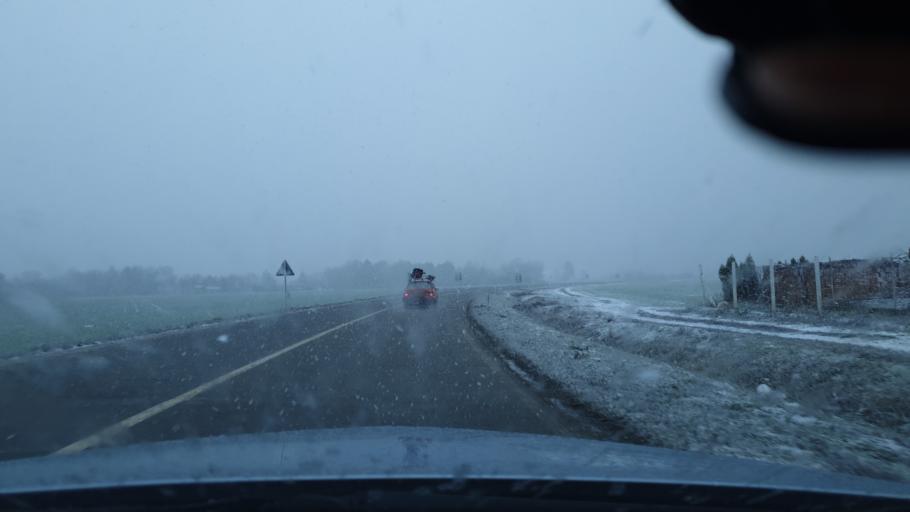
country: RS
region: Autonomna Pokrajina Vojvodina
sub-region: Juznobanatski Okrug
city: Pancevo
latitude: 44.8685
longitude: 20.7301
